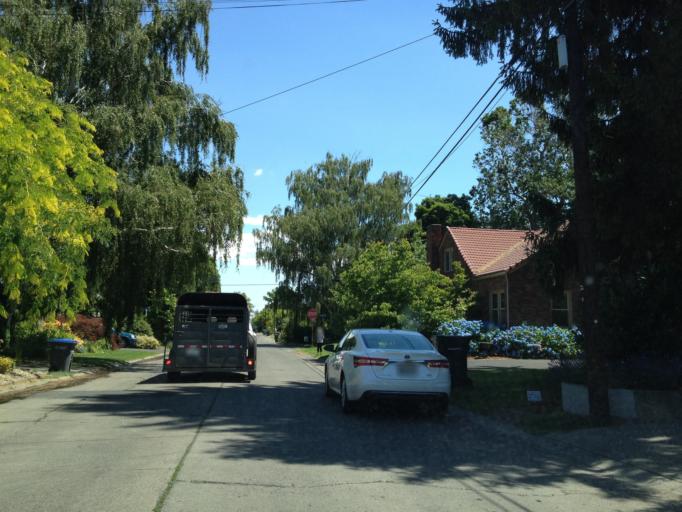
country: US
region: Washington
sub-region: Yakima County
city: Yakima
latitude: 46.5972
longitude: -120.5471
